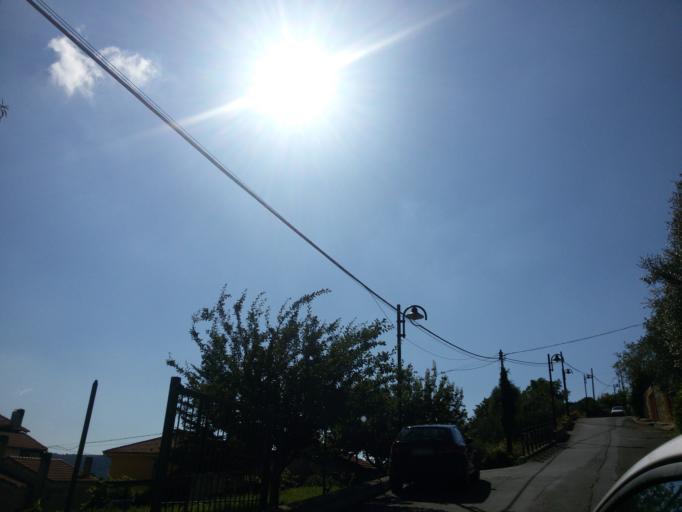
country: IT
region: Liguria
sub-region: Provincia di Savona
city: Borgio
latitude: 44.1801
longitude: 8.3018
